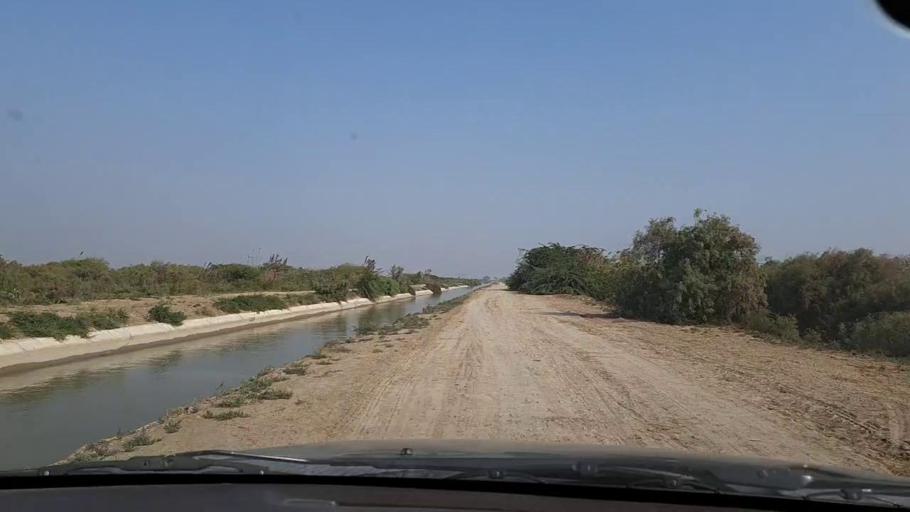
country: PK
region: Sindh
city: Mirpur Sakro
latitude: 24.3419
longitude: 67.7135
